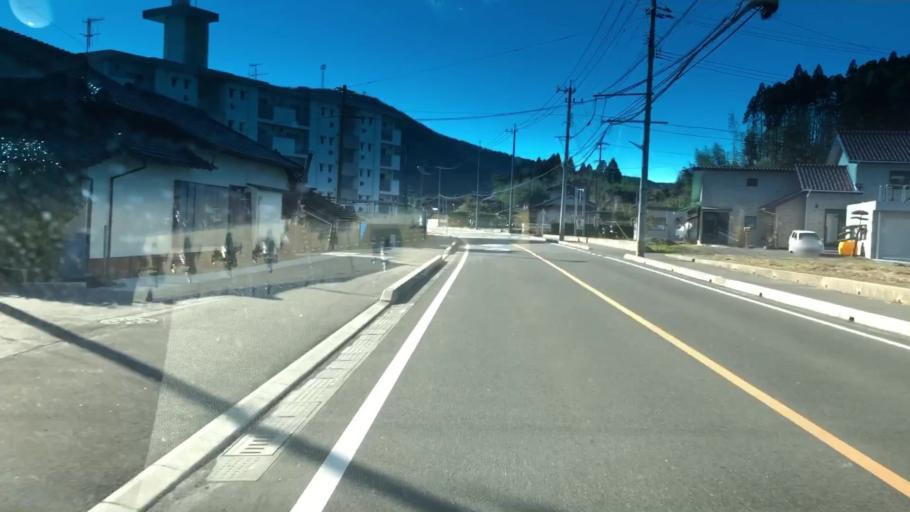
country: JP
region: Kagoshima
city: Satsumasendai
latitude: 31.8170
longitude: 130.2759
